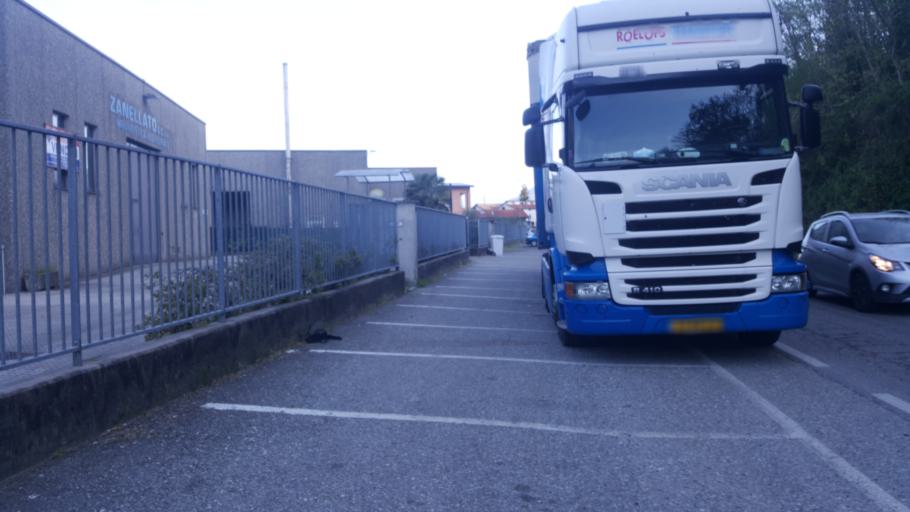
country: IT
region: Lombardy
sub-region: Provincia di Varese
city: Montegrino Valtravaglia
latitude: 45.9814
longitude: 8.7496
